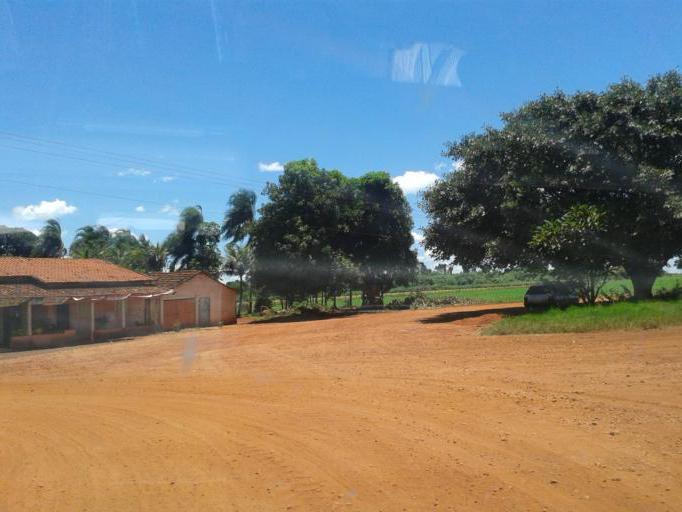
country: BR
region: Minas Gerais
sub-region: Capinopolis
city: Capinopolis
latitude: -18.5968
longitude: -49.5200
